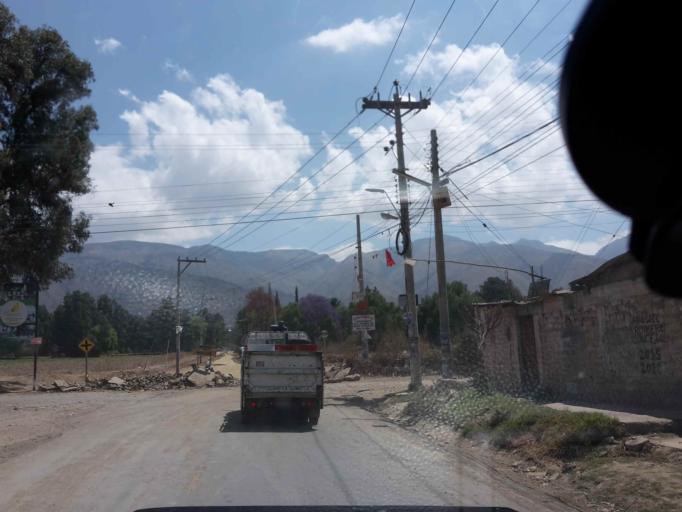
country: BO
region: Cochabamba
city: Cochabamba
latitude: -17.3491
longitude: -66.2249
